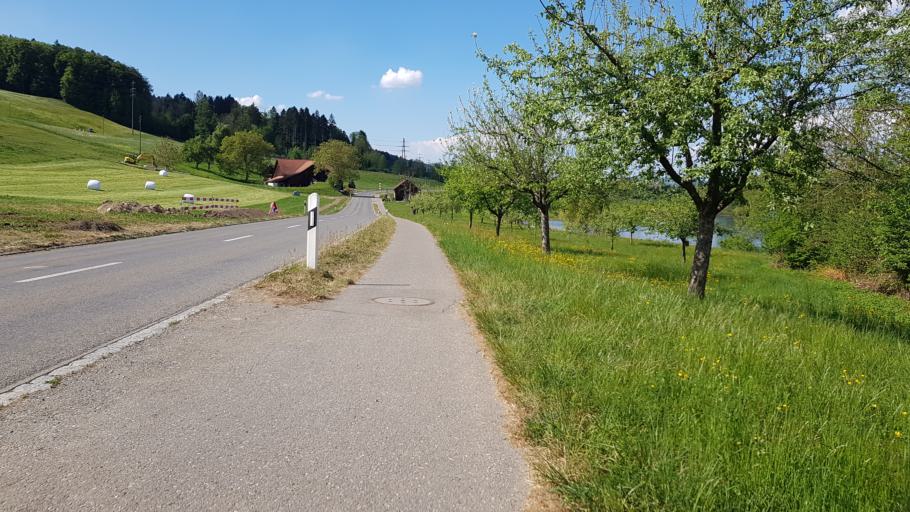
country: CH
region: Lucerne
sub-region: Hochdorf District
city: Hitzkirch
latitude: 47.2061
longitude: 8.2443
